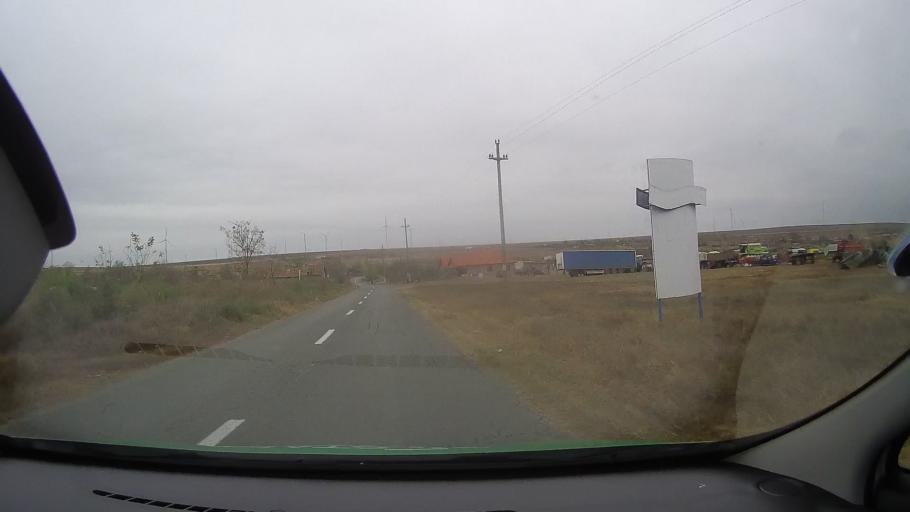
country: RO
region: Constanta
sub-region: Comuna Pantelimon
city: Pantelimon
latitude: 44.4890
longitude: 28.3624
